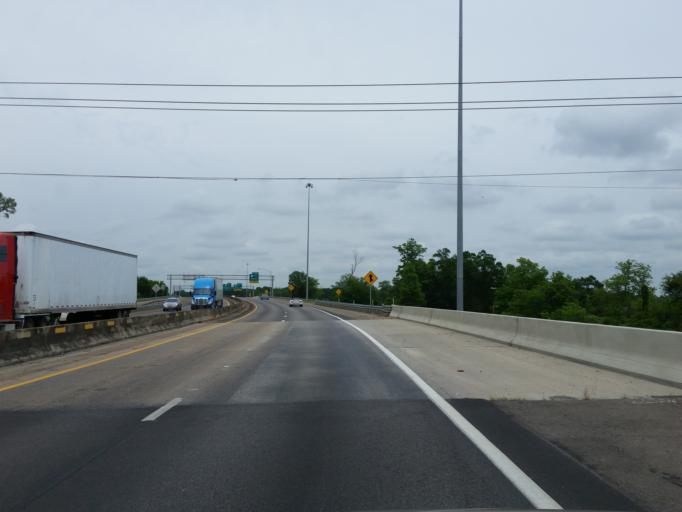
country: US
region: Mississippi
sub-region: Jones County
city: Laurel
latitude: 31.6853
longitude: -89.1286
